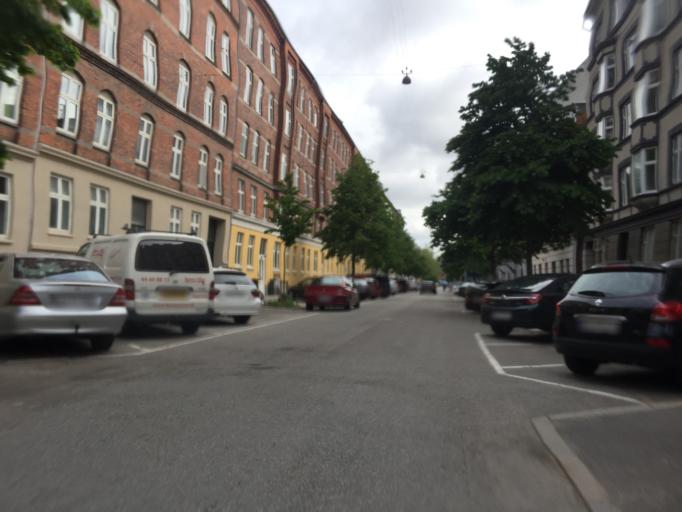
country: DK
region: Capital Region
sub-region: Frederiksberg Kommune
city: Frederiksberg
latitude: 55.6835
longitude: 12.5290
